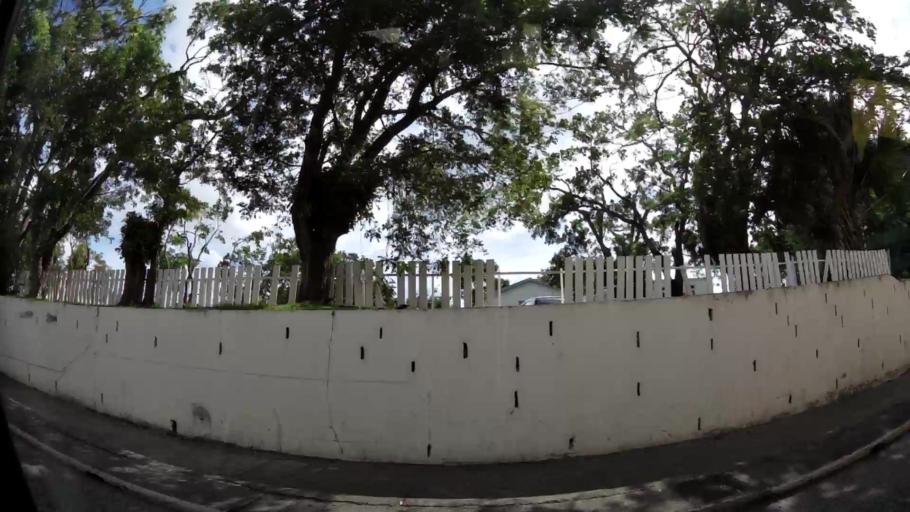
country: BB
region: Saint Michael
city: Bridgetown
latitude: 13.0940
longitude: -59.5988
